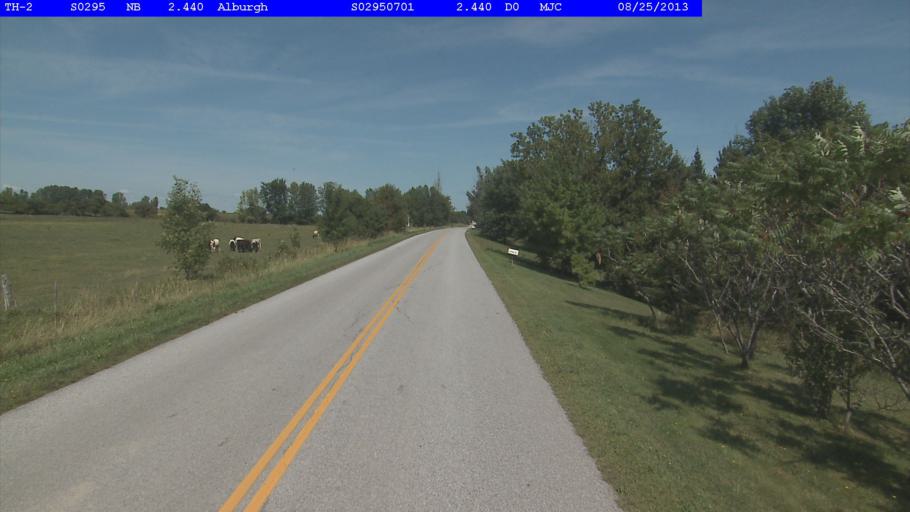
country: US
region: Vermont
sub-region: Franklin County
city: Swanton
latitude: 45.0071
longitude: -73.2141
